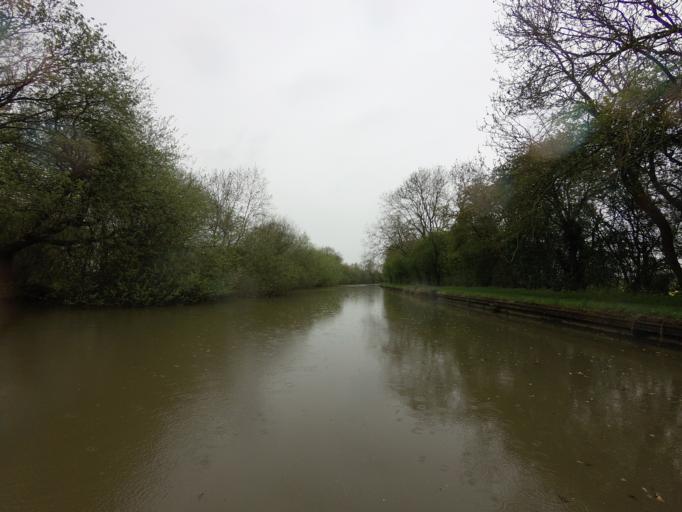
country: GB
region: England
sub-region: Milton Keynes
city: Castlethorpe
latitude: 52.0885
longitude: -0.8604
